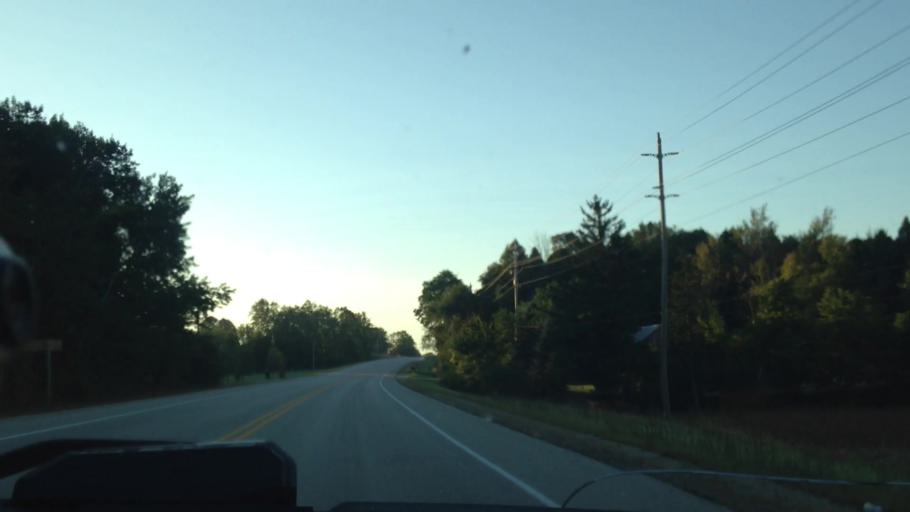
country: US
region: Wisconsin
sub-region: Washington County
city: Newburg
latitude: 43.4233
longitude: -88.0302
